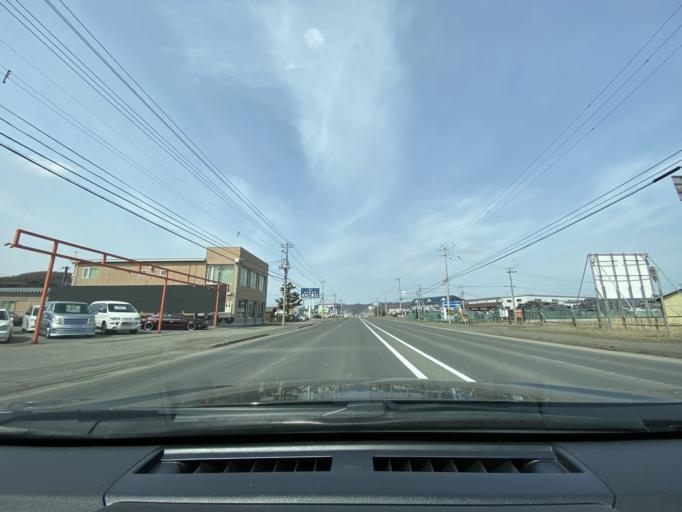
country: JP
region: Hokkaido
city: Kitami
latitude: 43.8002
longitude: 143.8255
